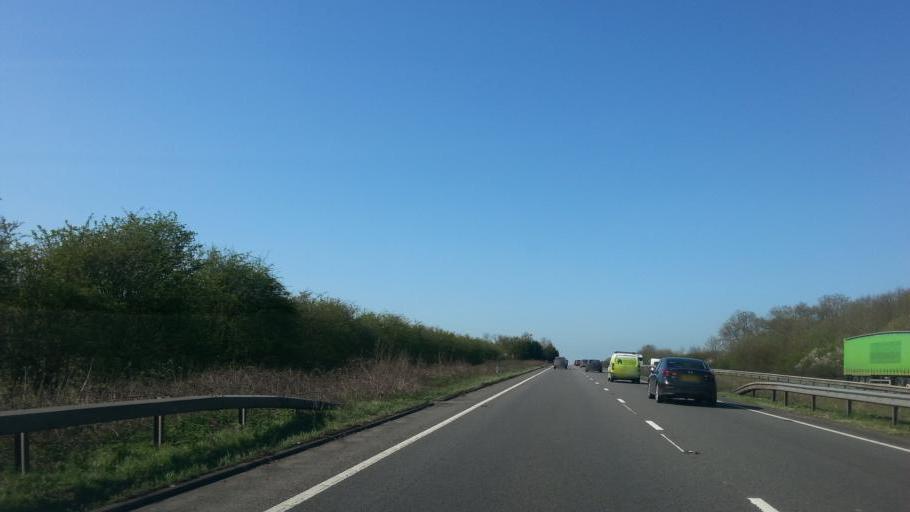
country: GB
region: England
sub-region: District of Rutland
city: Clipsham
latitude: 52.7202
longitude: -0.5953
